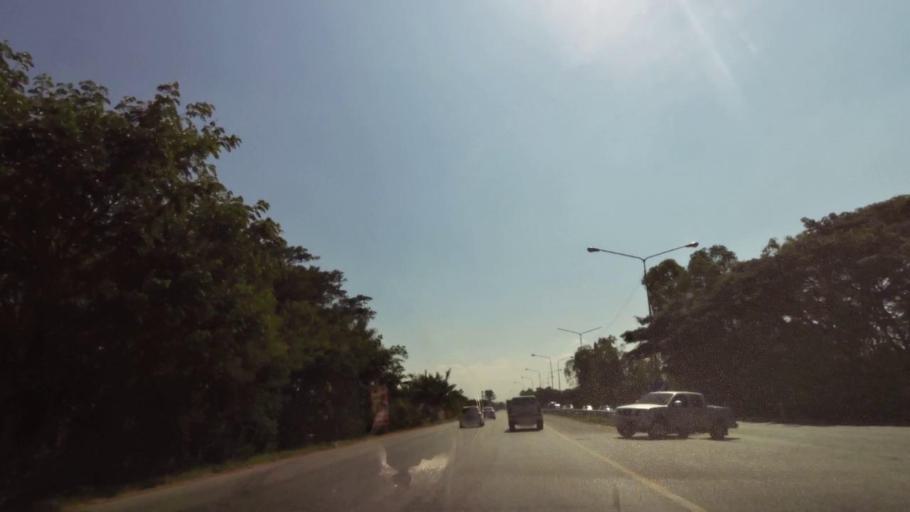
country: TH
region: Nakhon Sawan
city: Nakhon Sawan
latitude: 15.7815
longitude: 100.1212
